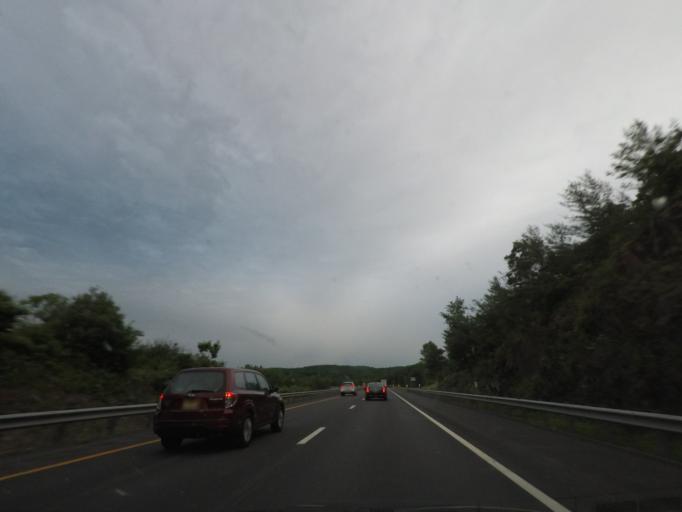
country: US
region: New York
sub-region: Columbia County
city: Chatham
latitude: 42.4361
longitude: -73.5546
